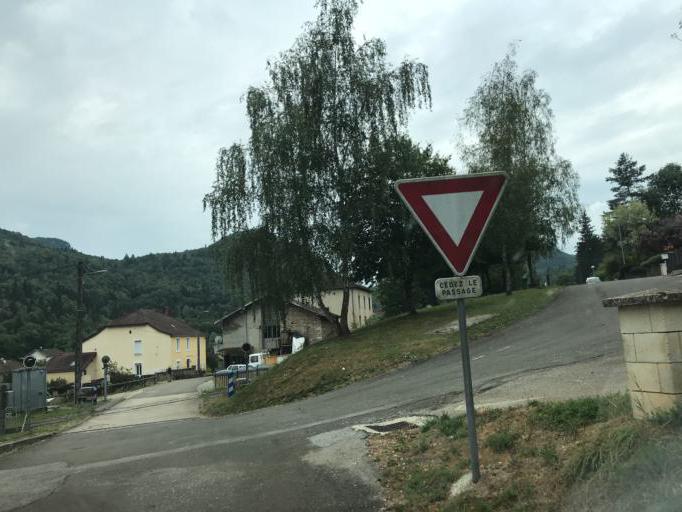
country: FR
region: Franche-Comte
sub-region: Departement du Jura
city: Lavans-les-Saint-Claude
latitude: 46.3612
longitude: 5.7859
